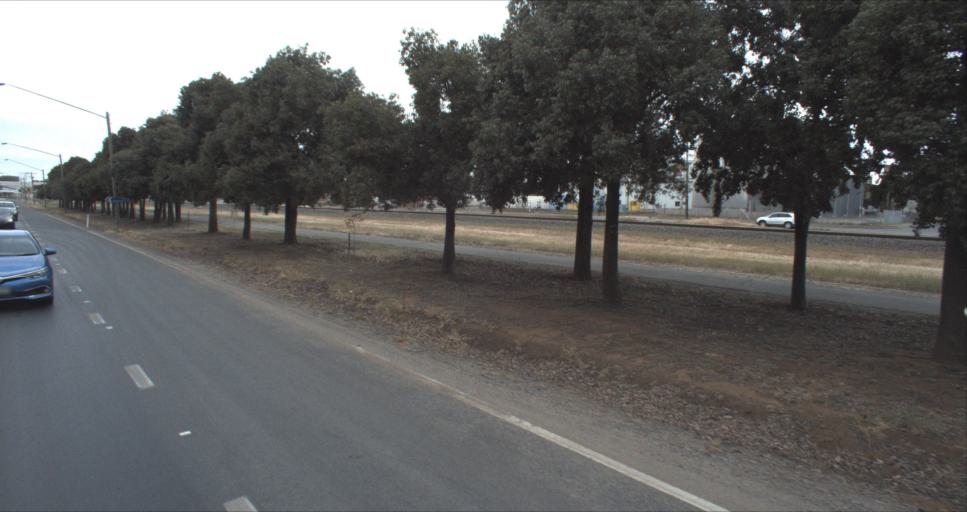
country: AU
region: New South Wales
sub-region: Leeton
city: Leeton
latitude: -34.5510
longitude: 146.3880
